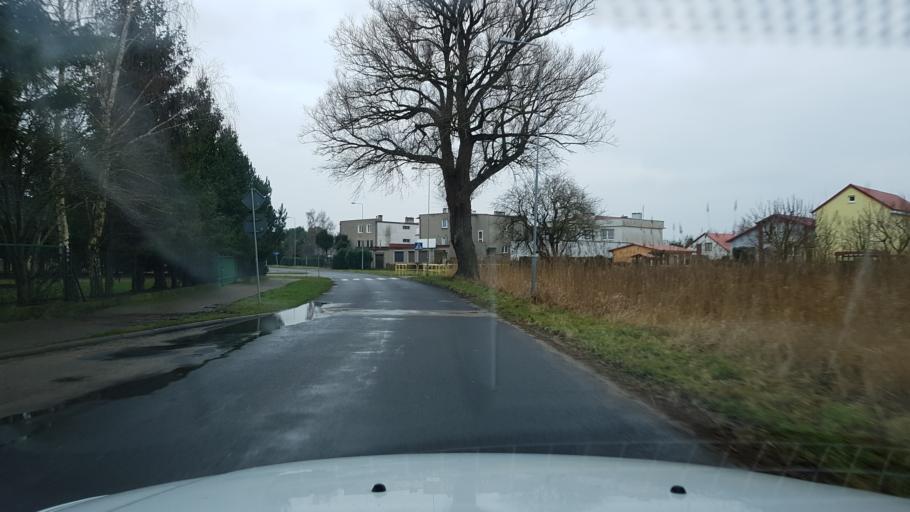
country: PL
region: West Pomeranian Voivodeship
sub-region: Powiat kolobrzeski
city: Grzybowo
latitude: 54.1584
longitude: 15.4820
